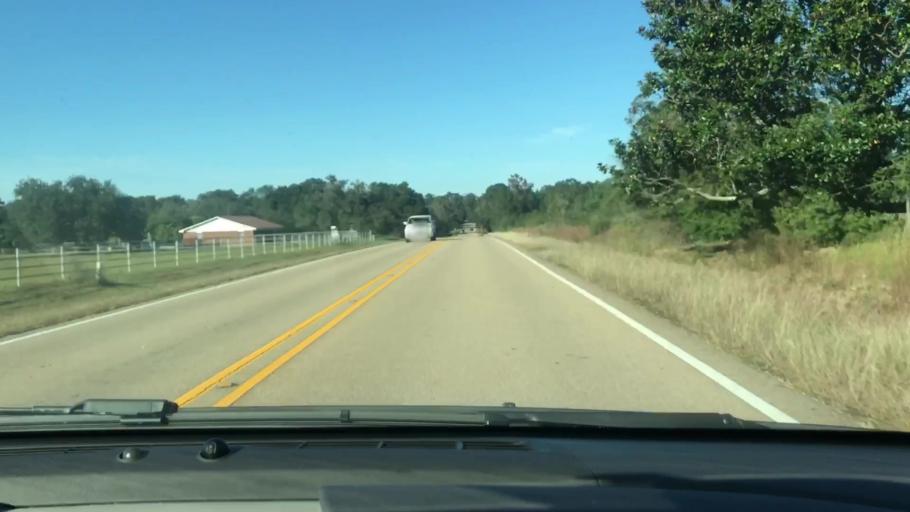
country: US
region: Louisiana
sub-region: Saint Tammany Parish
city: Abita Springs
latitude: 30.5415
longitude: -90.0452
